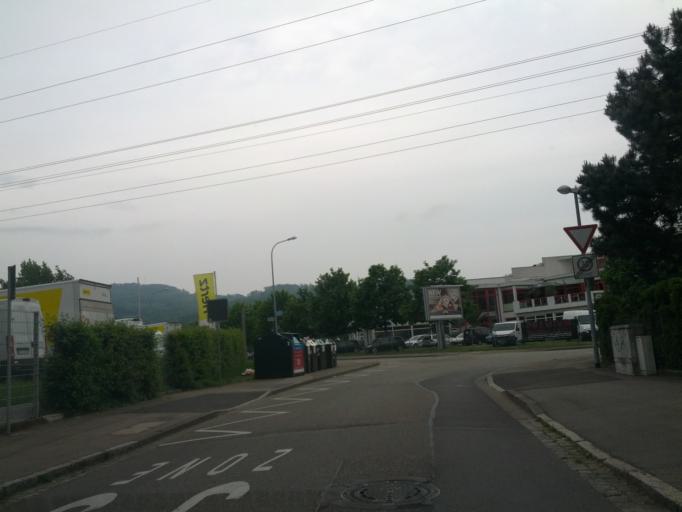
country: DE
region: Baden-Wuerttemberg
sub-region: Freiburg Region
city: Merzhausen
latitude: 47.9869
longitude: 7.8027
